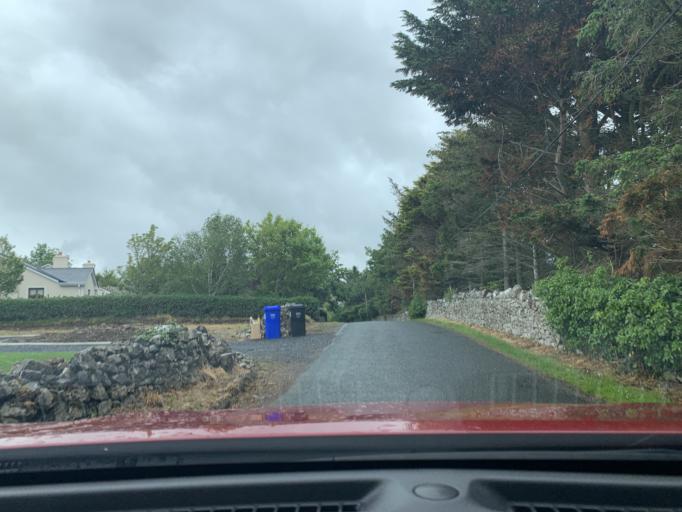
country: IE
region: Connaught
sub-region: Sligo
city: Sligo
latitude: 54.2981
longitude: -8.4599
